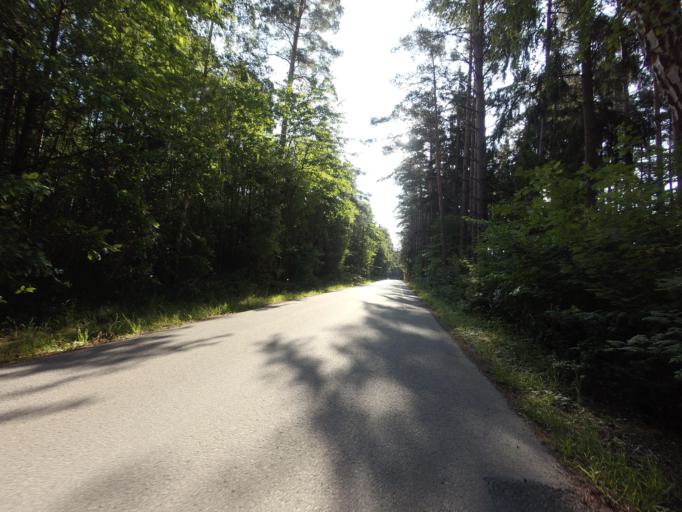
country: SE
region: Skane
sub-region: Kavlinge Kommun
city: Hofterup
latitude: 55.8325
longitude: 12.9480
